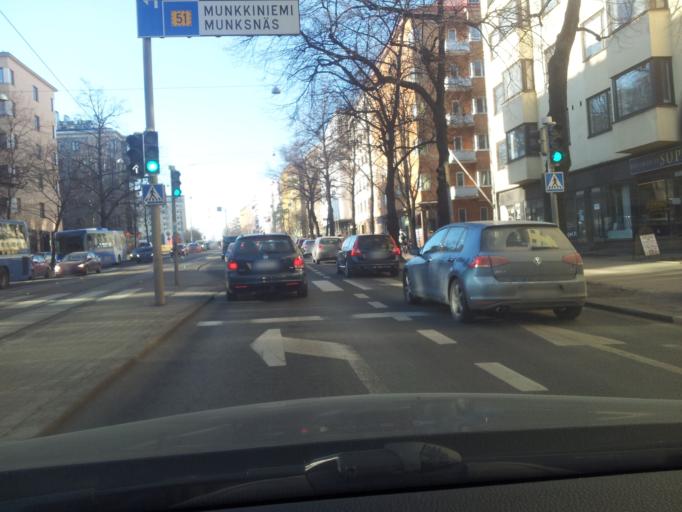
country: FI
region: Uusimaa
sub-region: Helsinki
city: Helsinki
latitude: 60.1904
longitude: 24.9150
